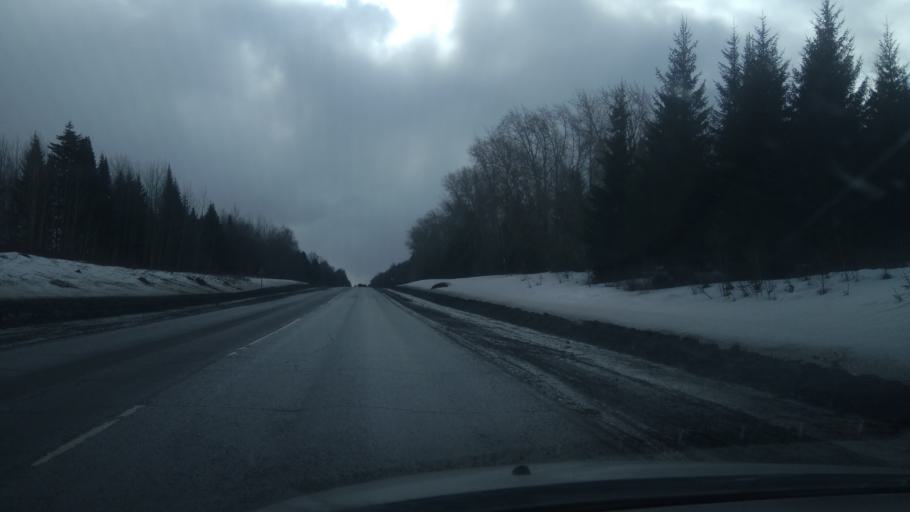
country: RU
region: Perm
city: Kukushtan
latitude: 57.6224
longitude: 56.4788
